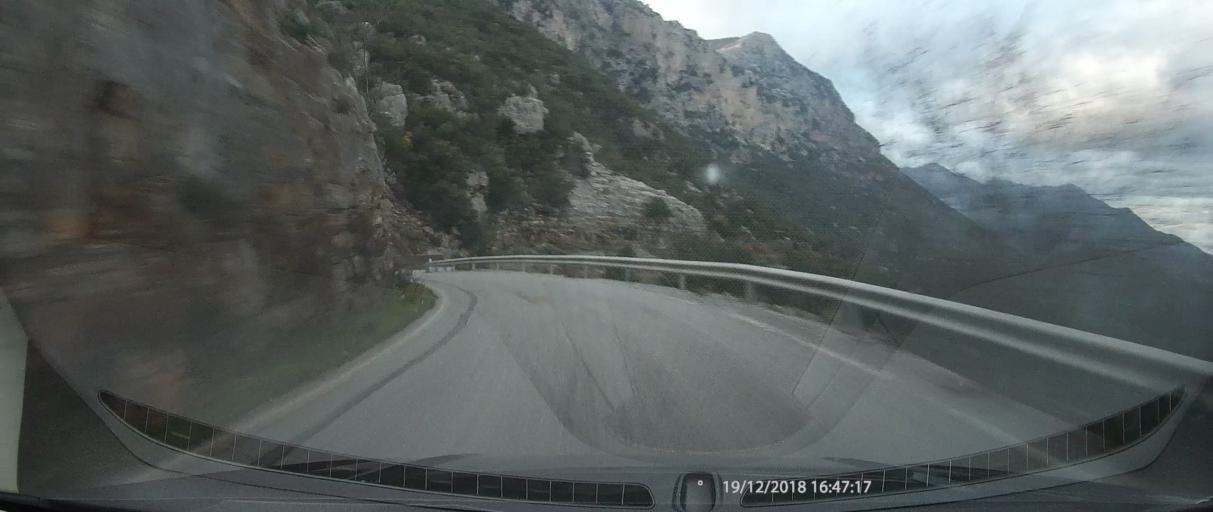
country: GR
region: Peloponnese
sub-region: Nomos Lakonias
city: Sykea
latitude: 36.9281
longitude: 23.0053
